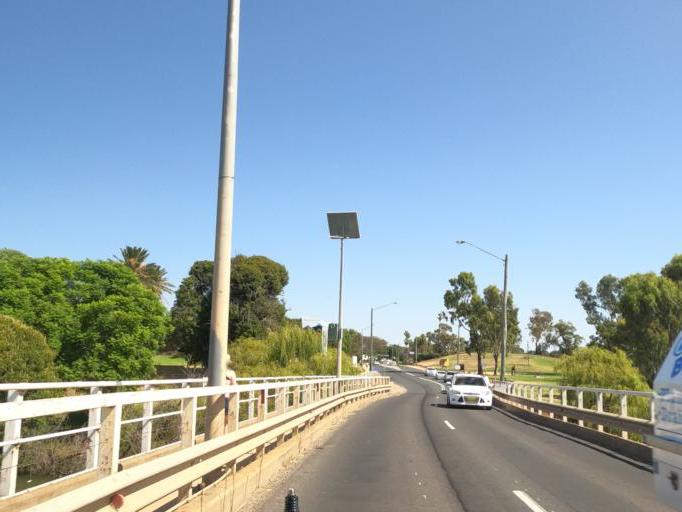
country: AU
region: New South Wales
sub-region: Corowa Shire
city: Mulwala
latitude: -36.0038
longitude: 146.0037
